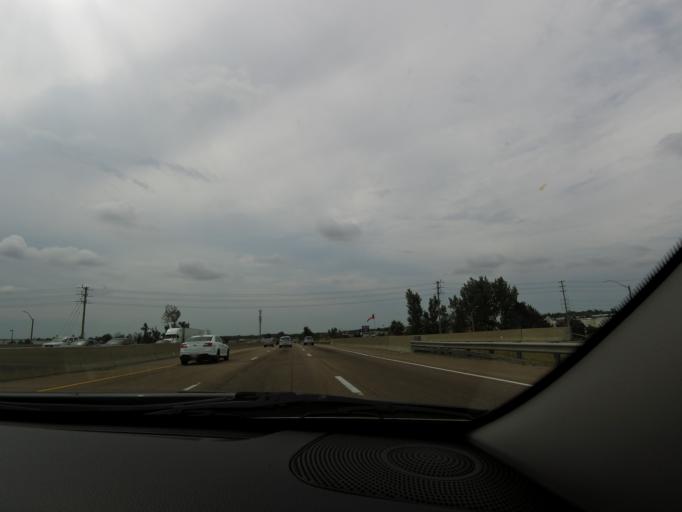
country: CA
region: Ontario
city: Innisfil
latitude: 44.3359
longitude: -79.6850
